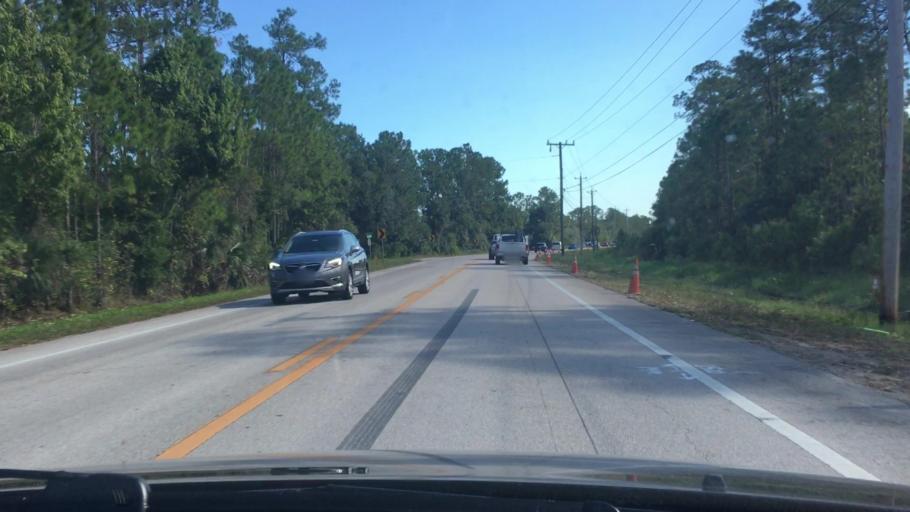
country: US
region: Florida
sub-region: Volusia County
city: Samsula-Spruce Creek
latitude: 29.1220
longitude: -81.0715
